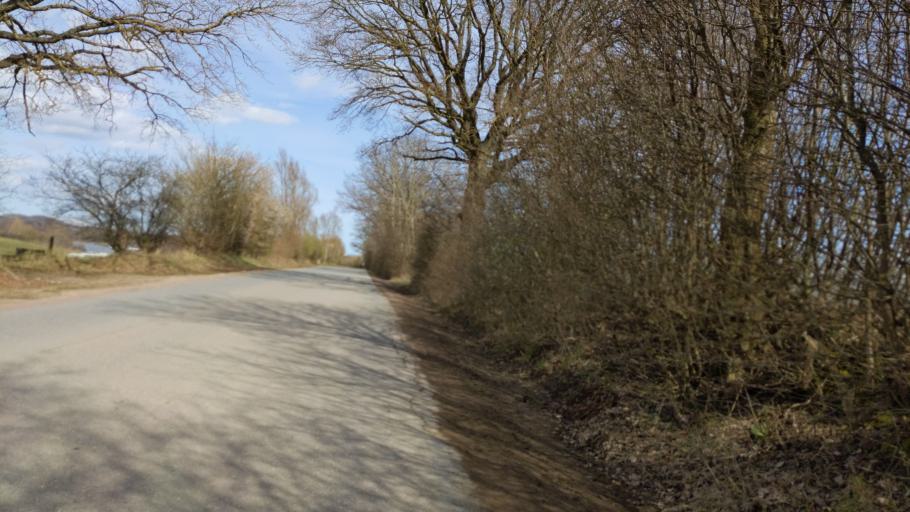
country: DE
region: Schleswig-Holstein
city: Susel
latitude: 54.0701
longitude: 10.6780
